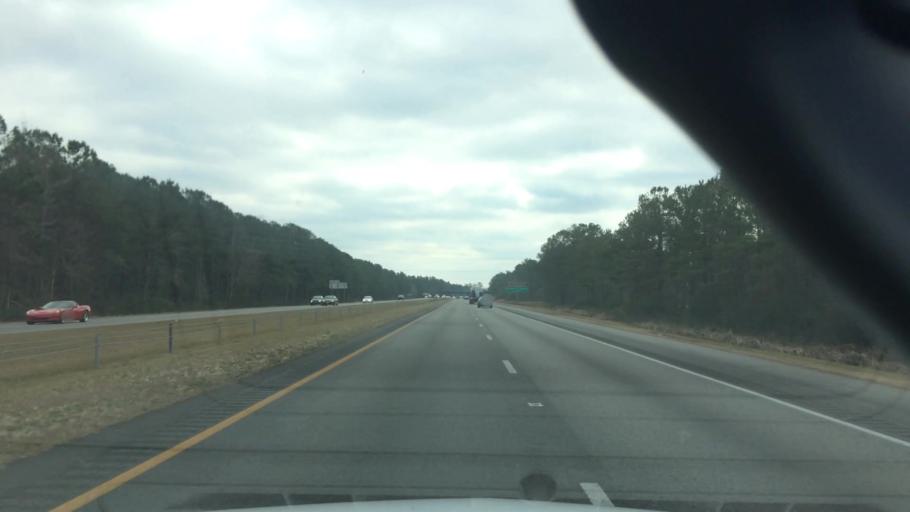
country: US
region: North Carolina
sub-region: New Hanover County
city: Skippers Corner
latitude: 34.3353
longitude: -77.8768
